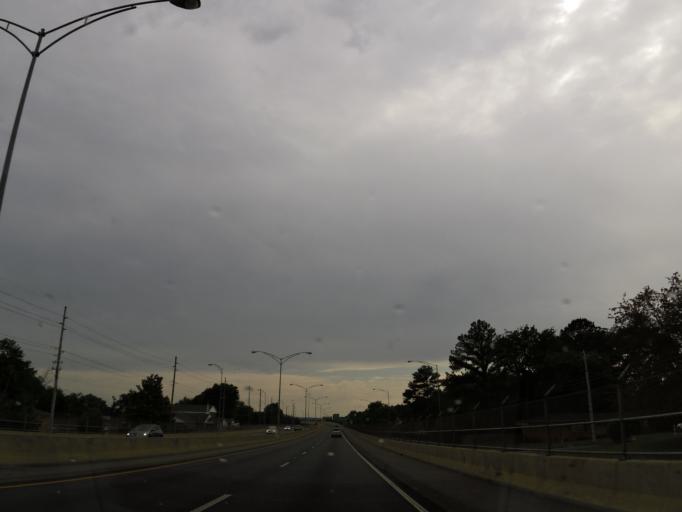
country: US
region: Alabama
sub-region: Madison County
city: Huntsville
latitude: 34.7540
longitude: -86.5711
